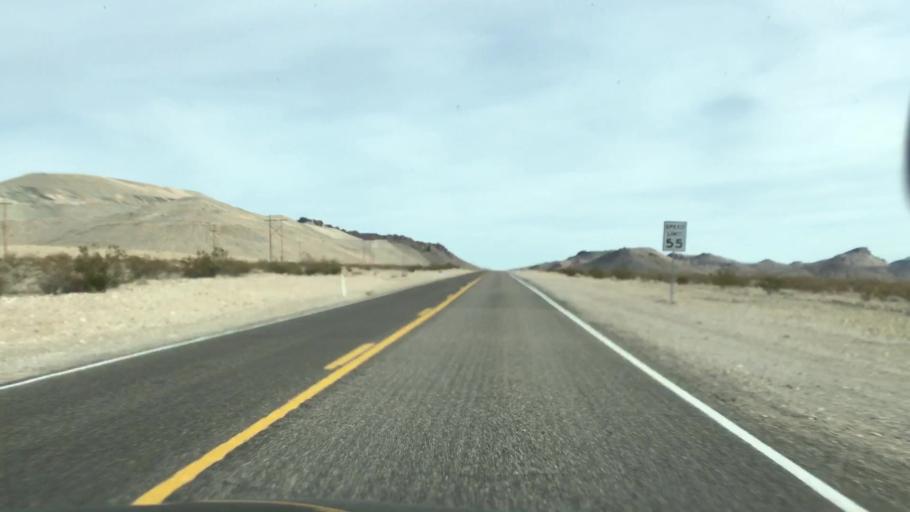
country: US
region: Nevada
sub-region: Nye County
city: Beatty
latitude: 36.8839
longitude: -116.8141
